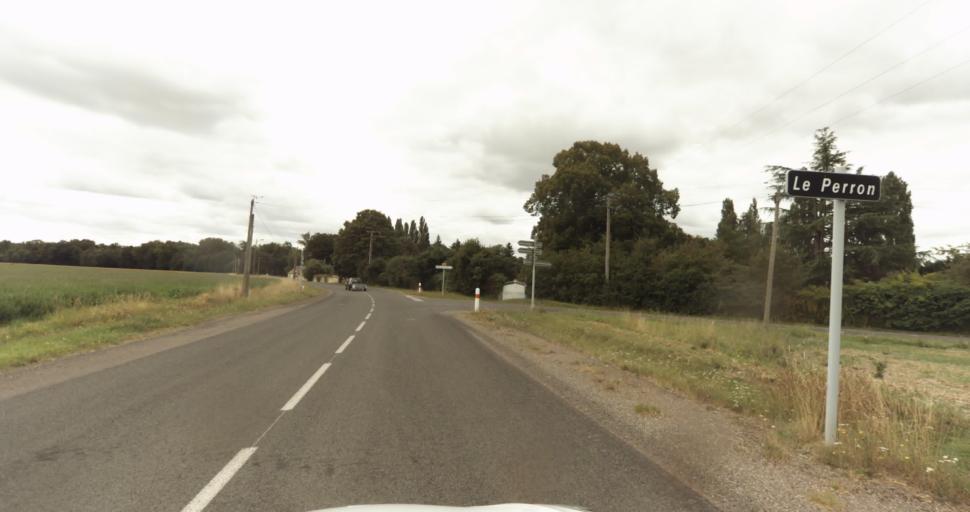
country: FR
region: Haute-Normandie
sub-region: Departement de l'Eure
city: La Madeleine-de-Nonancourt
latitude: 48.8310
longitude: 1.2272
